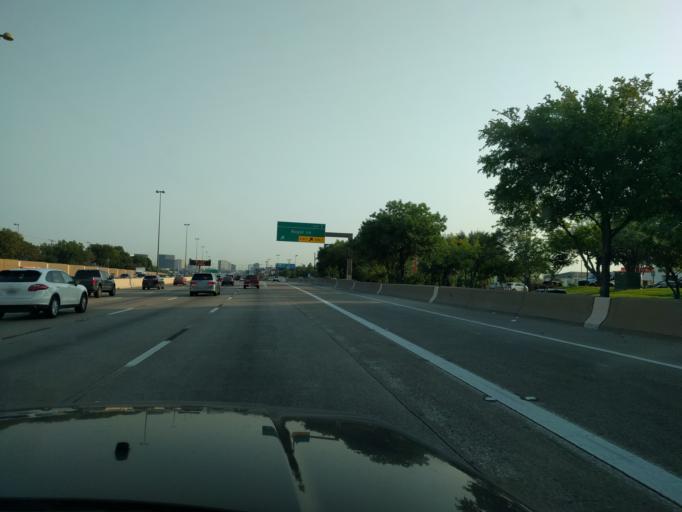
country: US
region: Texas
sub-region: Dallas County
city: University Park
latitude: 32.8923
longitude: -96.7690
